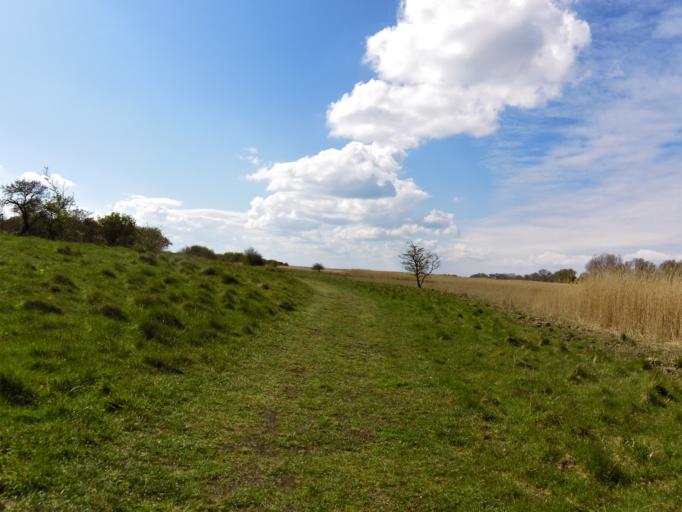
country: DE
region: Mecklenburg-Vorpommern
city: Hiddensee
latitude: 54.5983
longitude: 13.1422
